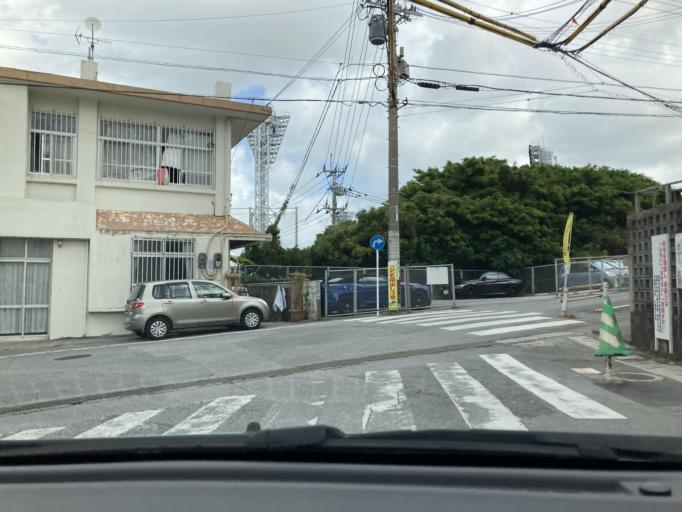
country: JP
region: Okinawa
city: Naha-shi
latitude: 26.2026
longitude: 127.6712
